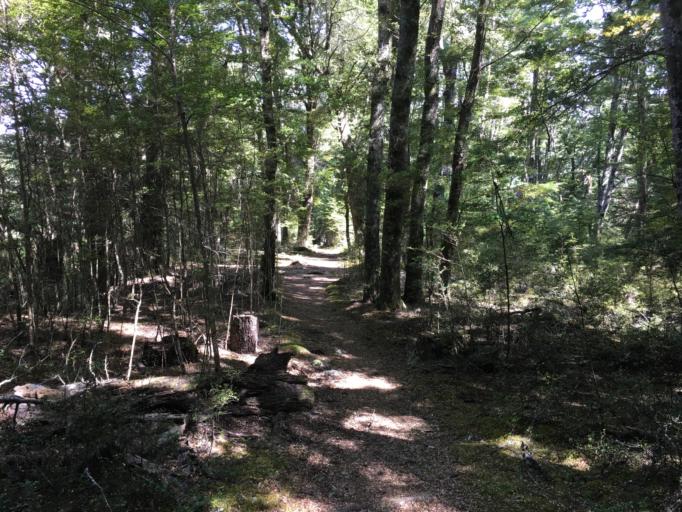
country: NZ
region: Southland
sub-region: Southland District
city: Te Anau
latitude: -45.4850
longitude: 167.6833
